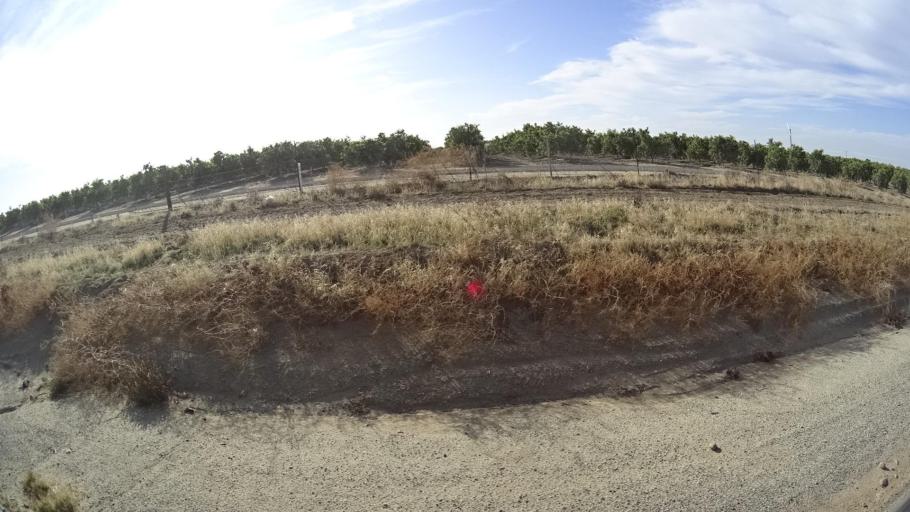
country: US
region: California
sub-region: Kern County
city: McFarland
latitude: 35.6025
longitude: -119.0782
